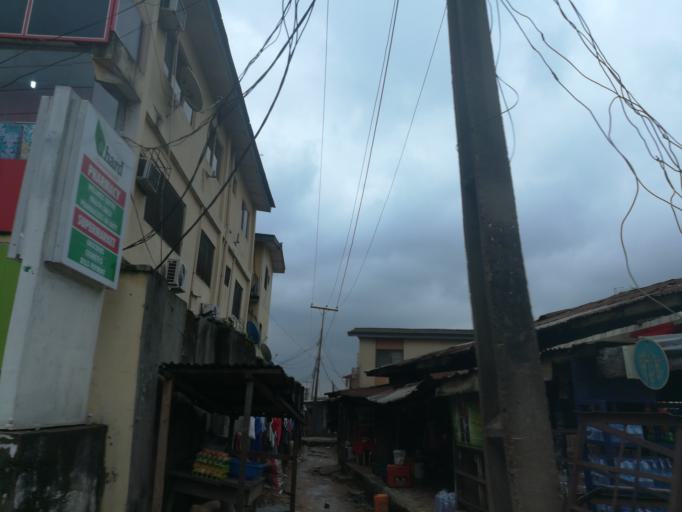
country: NG
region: Lagos
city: Ojota
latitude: 6.5710
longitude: 3.3711
